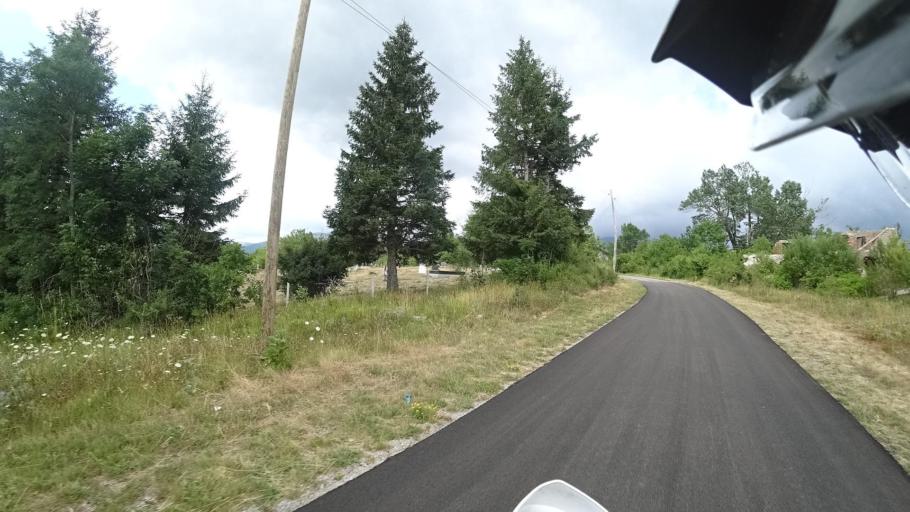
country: HR
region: Zadarska
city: Gracac
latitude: 44.5215
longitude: 15.8077
